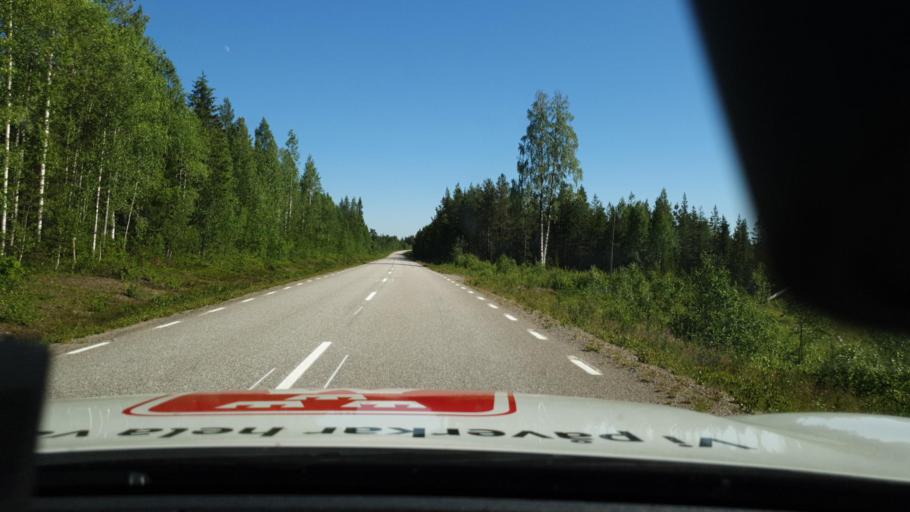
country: SE
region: Norrbotten
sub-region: Lulea Kommun
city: Ranea
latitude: 66.0117
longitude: 22.3071
